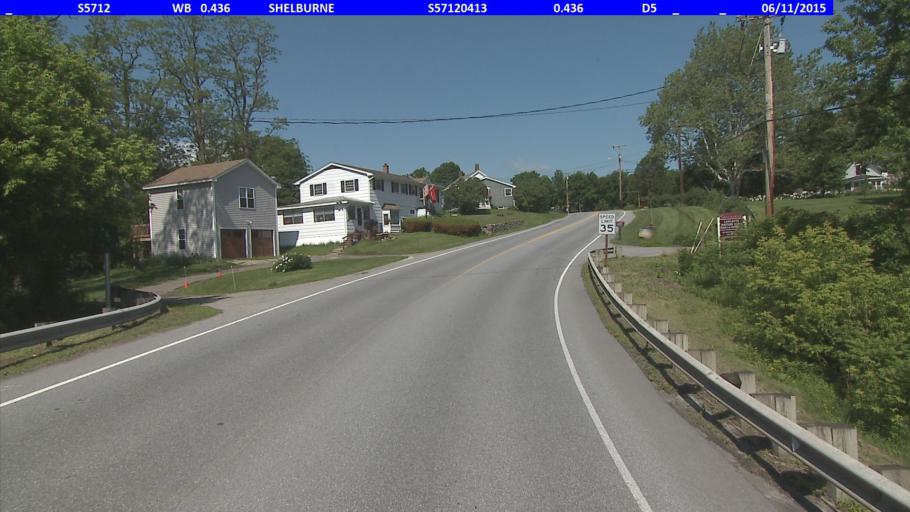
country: US
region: Vermont
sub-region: Chittenden County
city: Burlington
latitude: 44.3706
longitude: -73.2160
